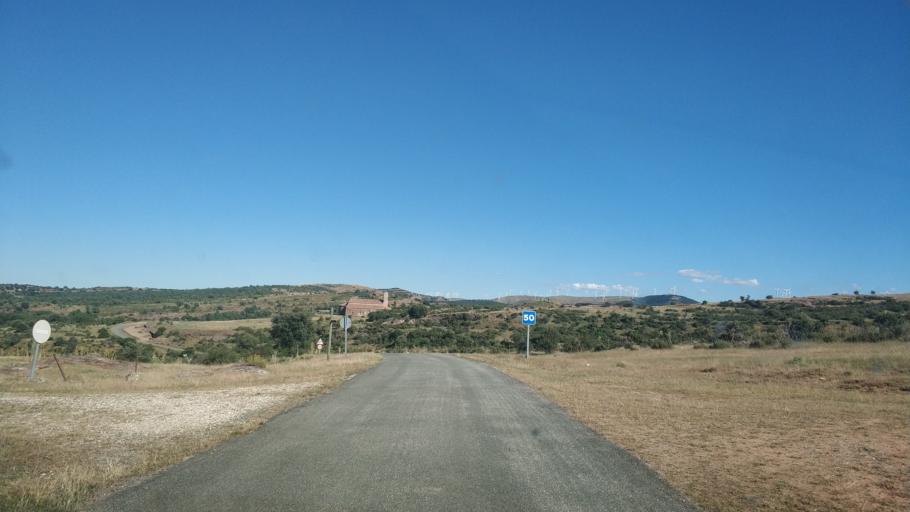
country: ES
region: Castille and Leon
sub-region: Provincia de Soria
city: Montejo de Tiermes
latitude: 41.3341
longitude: -3.1513
